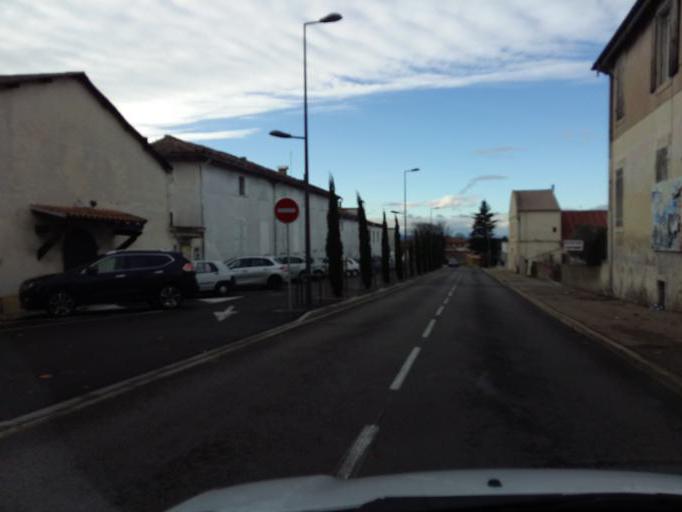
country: FR
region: Provence-Alpes-Cote d'Azur
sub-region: Departement du Vaucluse
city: Valreas
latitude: 44.3844
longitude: 4.9874
